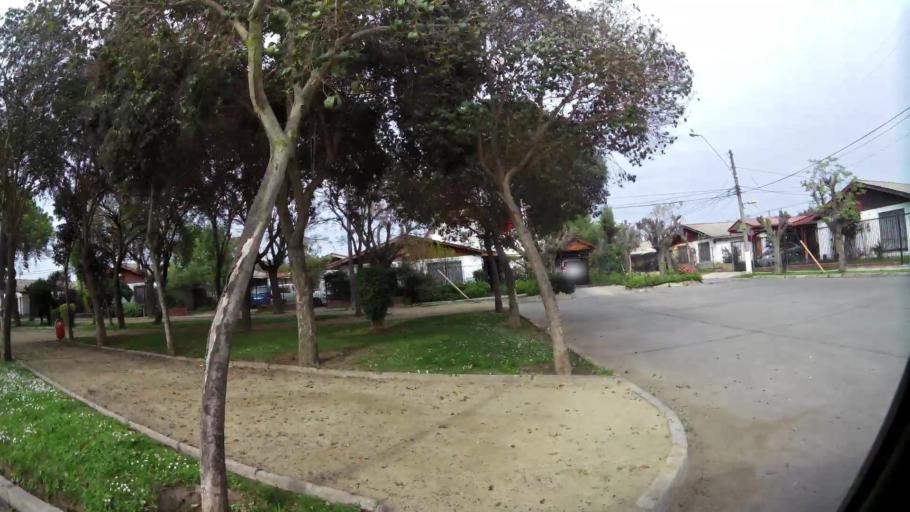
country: CL
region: Santiago Metropolitan
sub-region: Provincia de Santiago
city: Lo Prado
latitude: -33.5205
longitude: -70.7668
